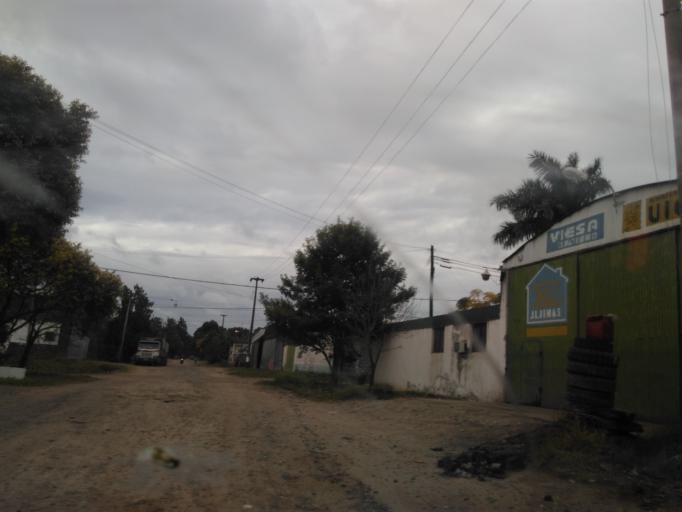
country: AR
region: Chaco
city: Fontana
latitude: -27.4372
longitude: -59.0156
